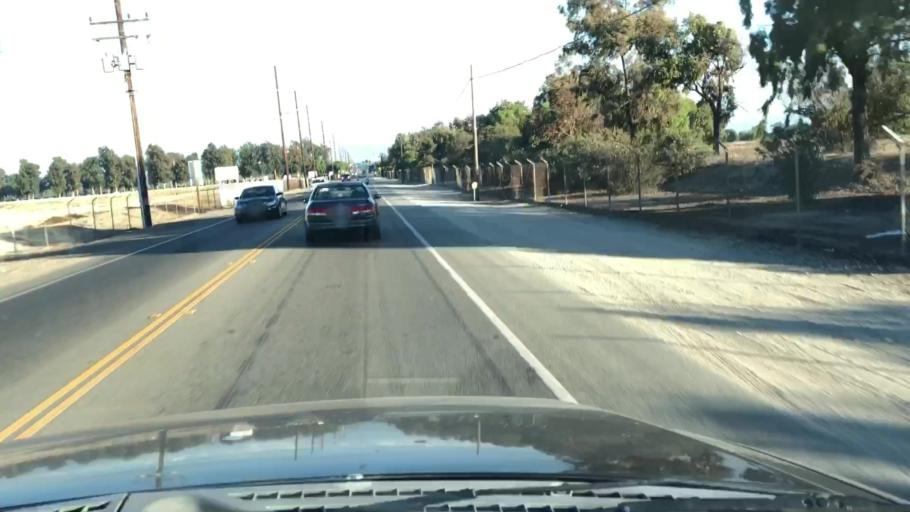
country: US
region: California
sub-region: Ventura County
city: Saticoy
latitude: 34.2706
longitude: -119.1320
